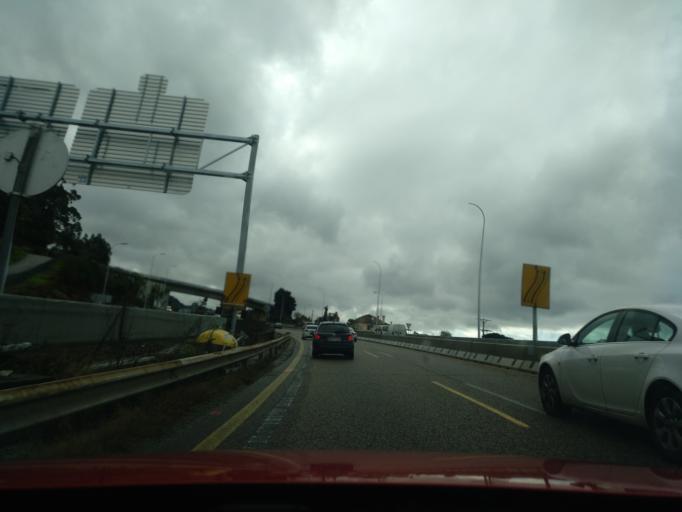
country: ES
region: Galicia
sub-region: Provincia de Pontevedra
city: Redondela
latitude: 42.2782
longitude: -8.6651
